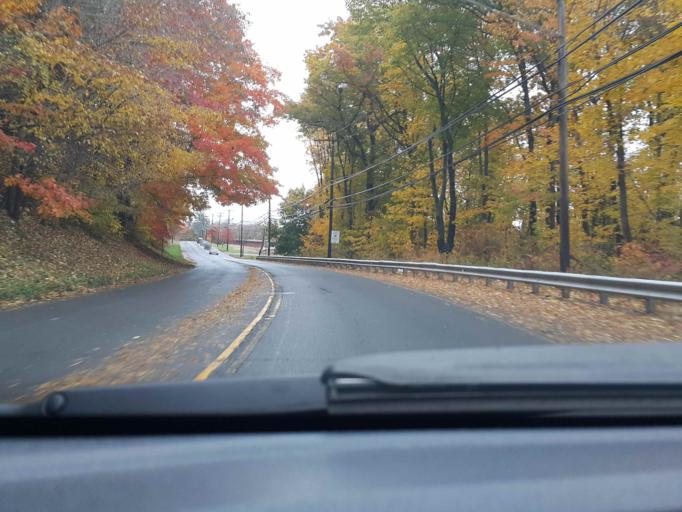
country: US
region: Connecticut
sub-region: Middlesex County
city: Middletown
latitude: 41.5327
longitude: -72.6577
